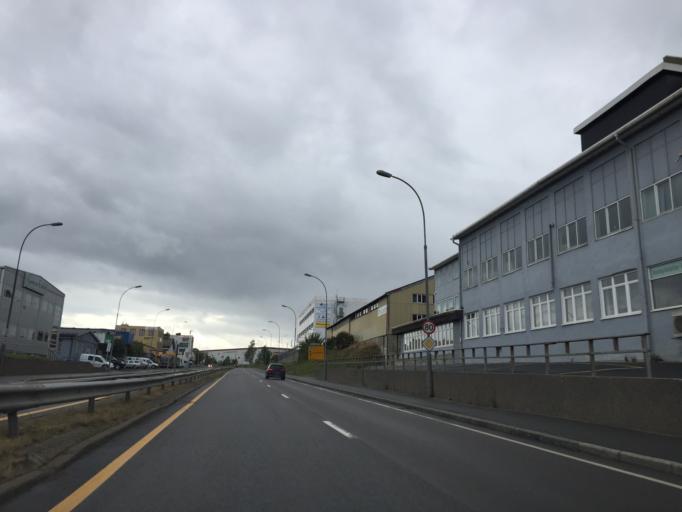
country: NO
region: Akershus
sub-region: Lorenskog
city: Kjenn
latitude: 59.9466
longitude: 10.8768
